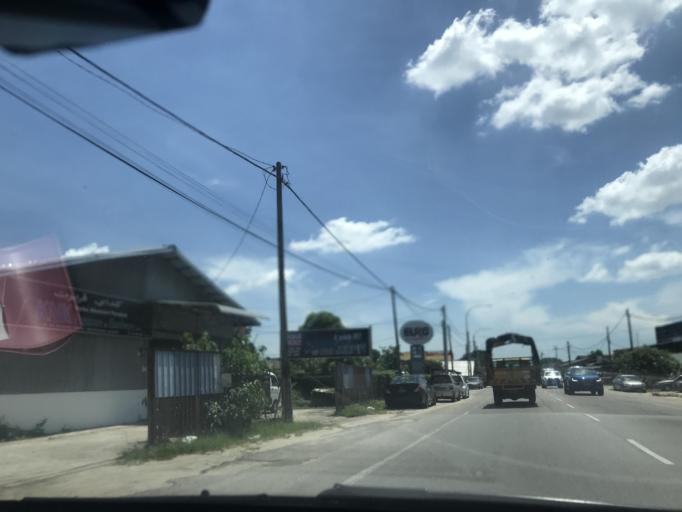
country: MY
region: Kelantan
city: Kota Bharu
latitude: 6.1196
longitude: 102.2704
